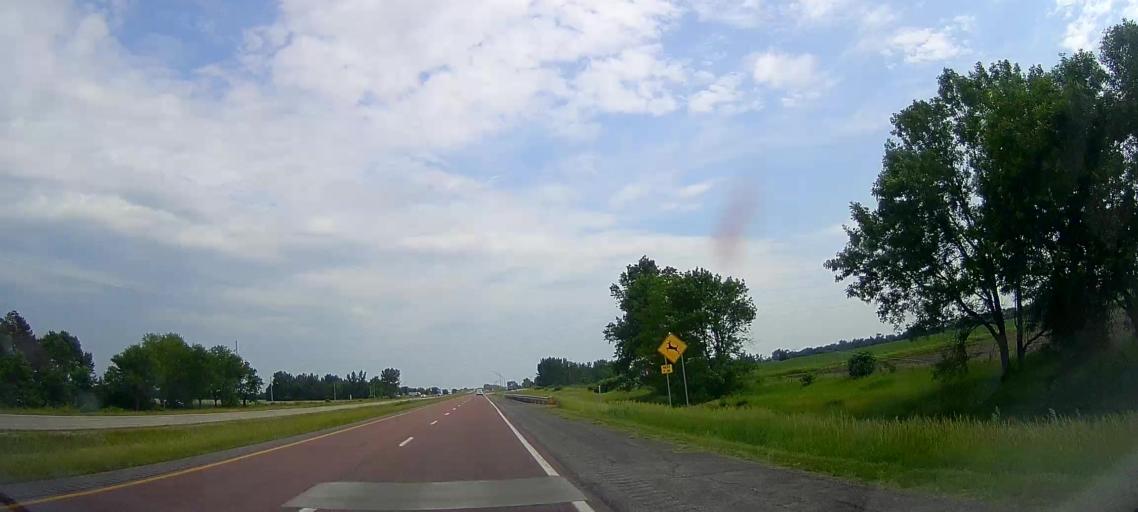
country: US
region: Iowa
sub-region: Monona County
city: Onawa
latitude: 41.9987
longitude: -96.1134
